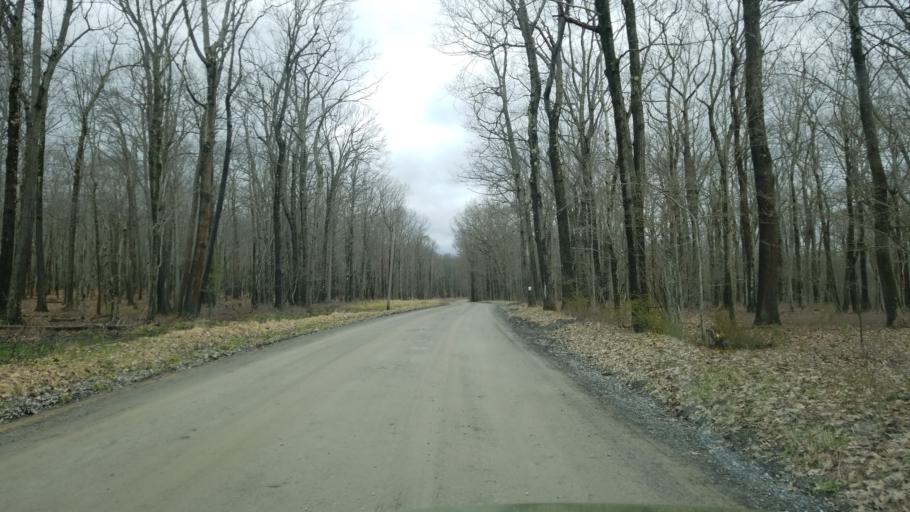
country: US
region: Pennsylvania
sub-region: Clearfield County
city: Shiloh
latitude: 41.1556
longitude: -78.3336
